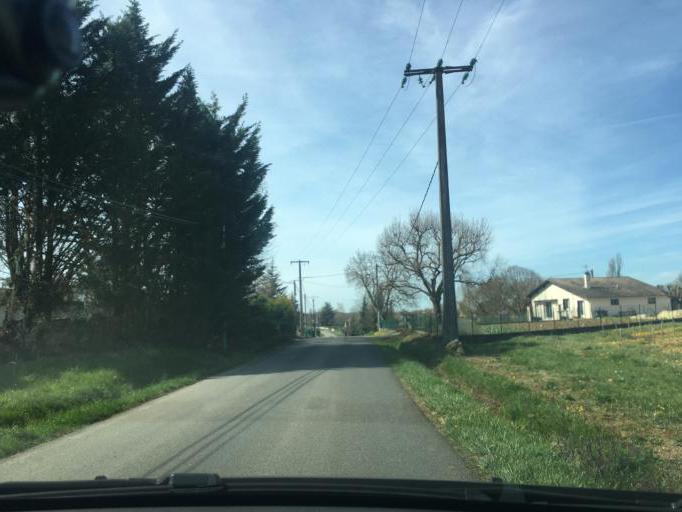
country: FR
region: Aquitaine
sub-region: Departement de la Gironde
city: Saint-Germain-du-Puch
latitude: 44.8481
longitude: -0.3505
